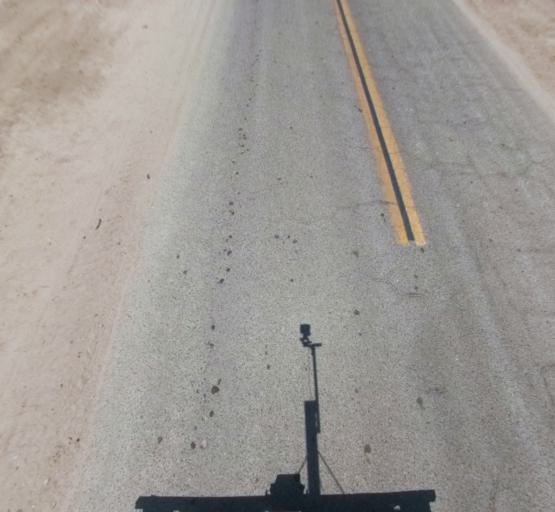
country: US
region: California
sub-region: Fresno County
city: Kerman
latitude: 36.8217
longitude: -120.1510
